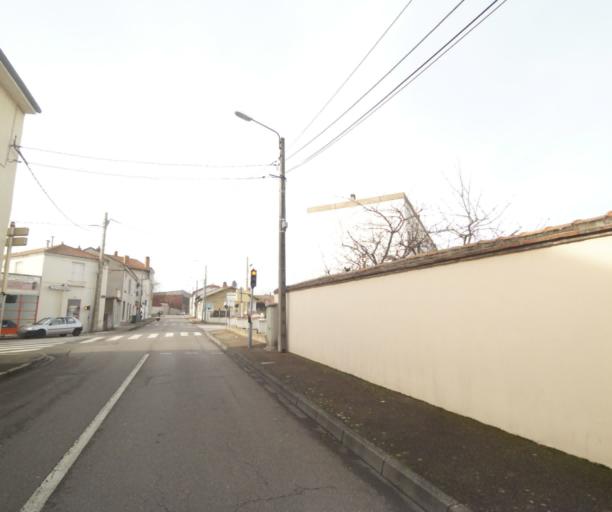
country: FR
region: Rhone-Alpes
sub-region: Departement de la Loire
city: Roanne
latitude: 46.0305
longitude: 4.0630
